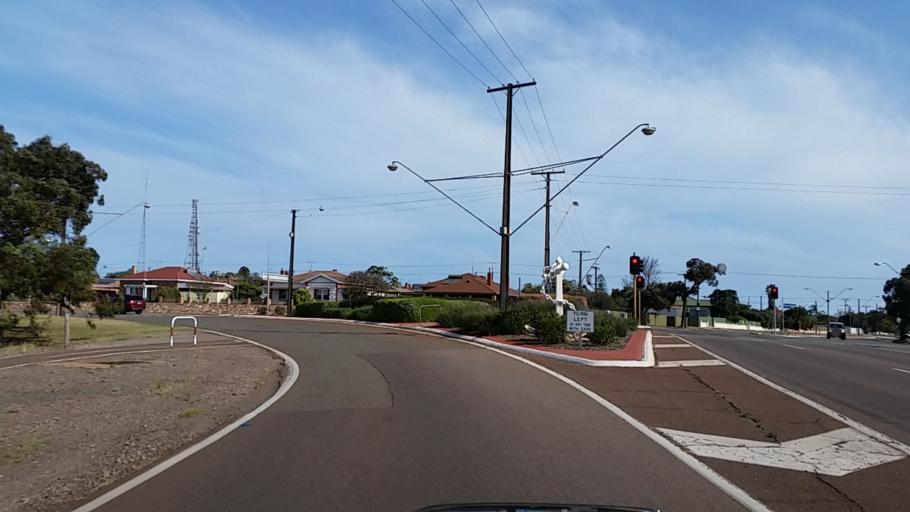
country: AU
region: South Australia
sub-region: Whyalla
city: Whyalla
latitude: -33.0249
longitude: 137.5723
